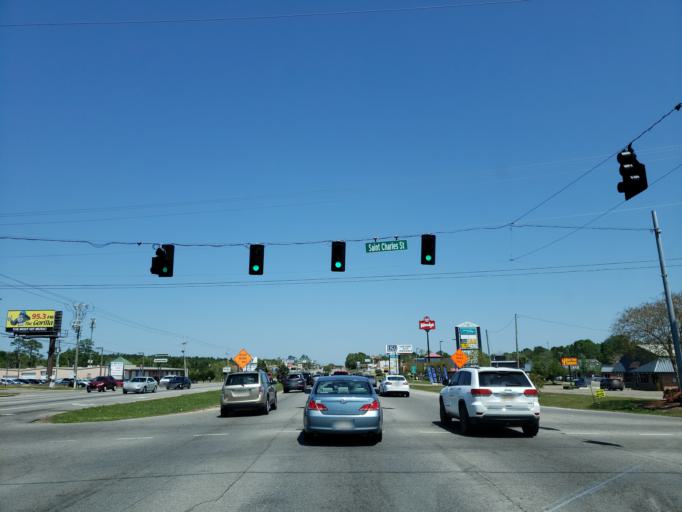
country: US
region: Mississippi
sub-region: Harrison County
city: Lyman
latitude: 30.4582
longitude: -89.1006
